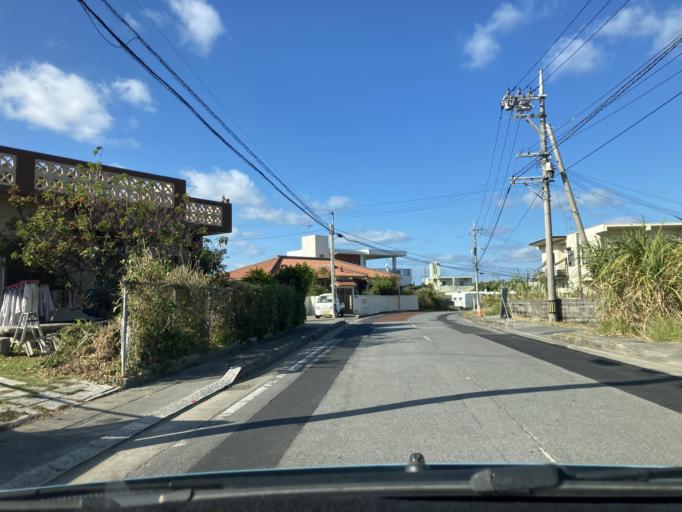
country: JP
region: Okinawa
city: Katsuren-haebaru
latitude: 26.3163
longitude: 127.9089
